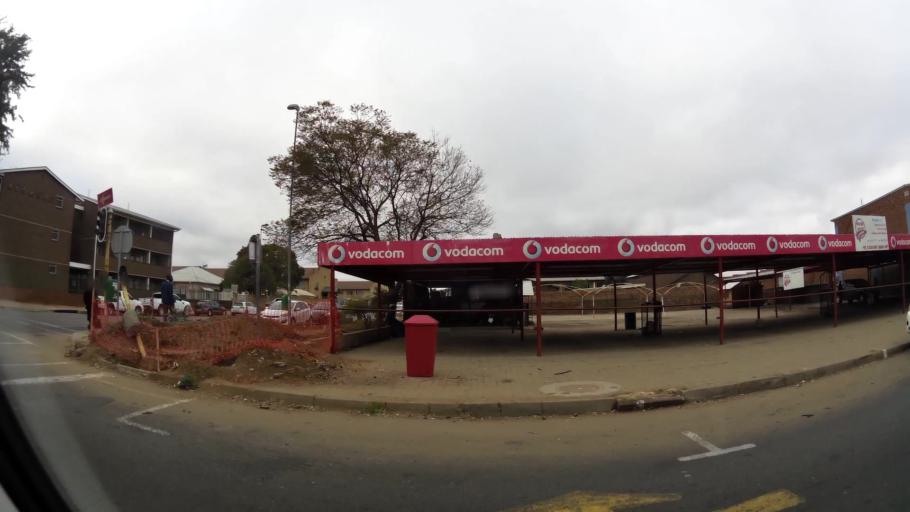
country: ZA
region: Limpopo
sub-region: Capricorn District Municipality
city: Polokwane
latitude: -23.9022
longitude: 29.4527
